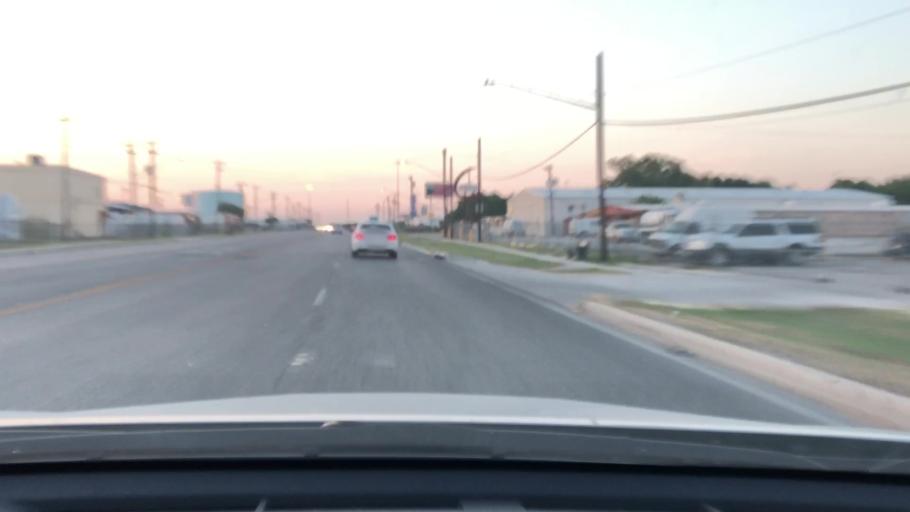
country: US
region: Texas
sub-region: Bexar County
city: Kirby
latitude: 29.4412
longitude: -98.4051
